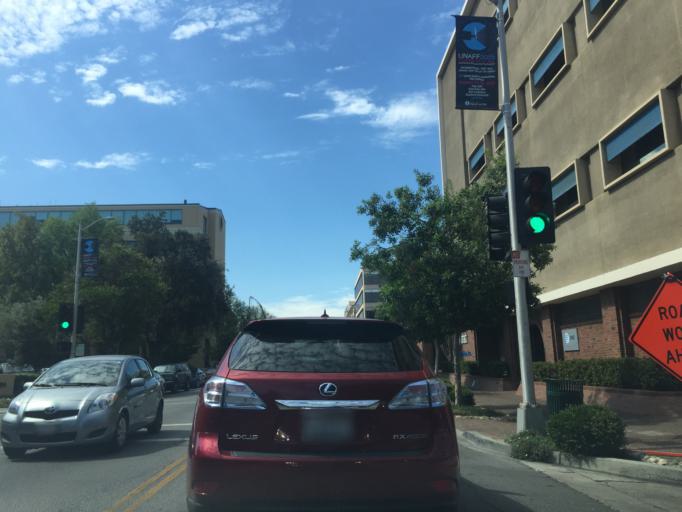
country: US
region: California
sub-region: Santa Clara County
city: Palo Alto
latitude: 37.4459
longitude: -122.1596
